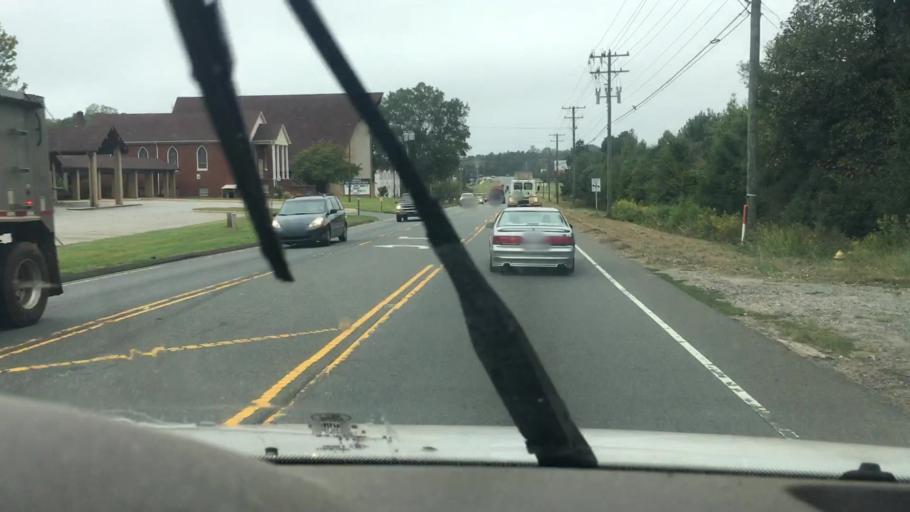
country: US
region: North Carolina
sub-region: Catawba County
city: Lake Norman of Catawba
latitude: 35.6026
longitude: -80.8990
